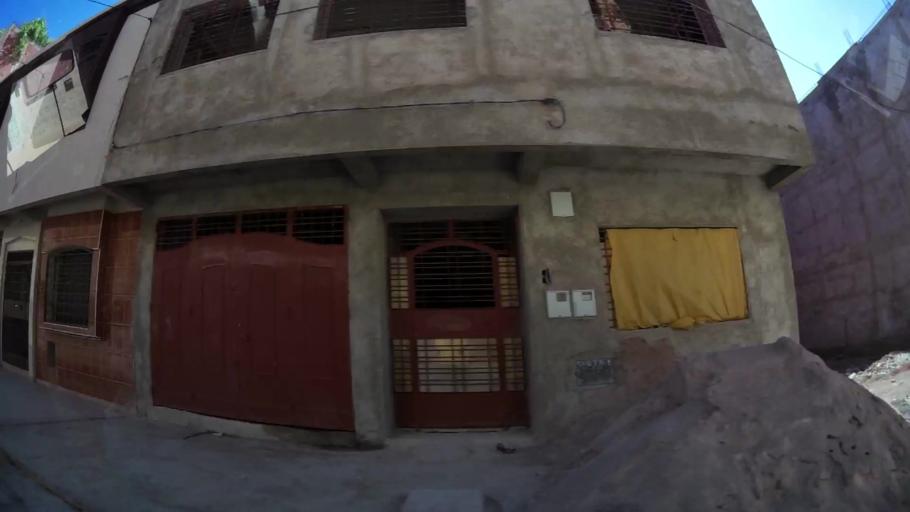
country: MA
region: Oriental
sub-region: Oujda-Angad
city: Oujda
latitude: 34.6861
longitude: -1.9427
